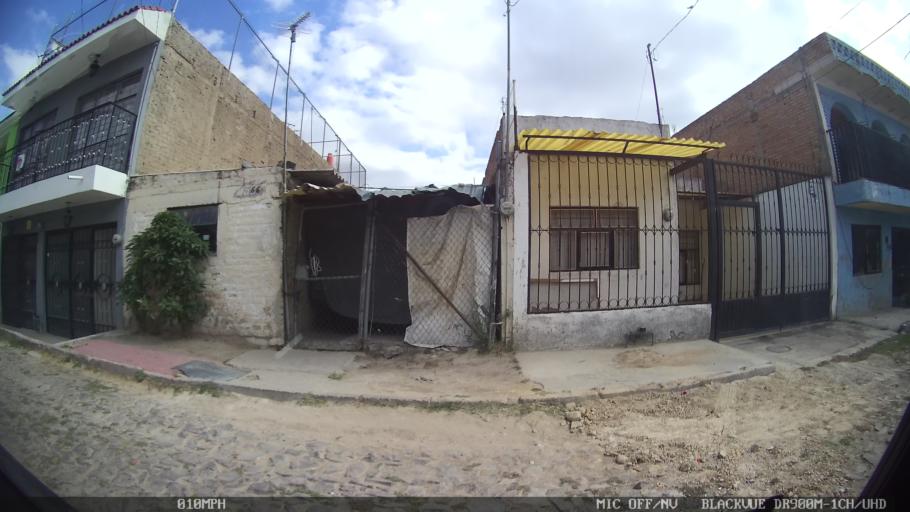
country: MX
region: Jalisco
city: Tlaquepaque
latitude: 20.6851
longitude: -103.2578
